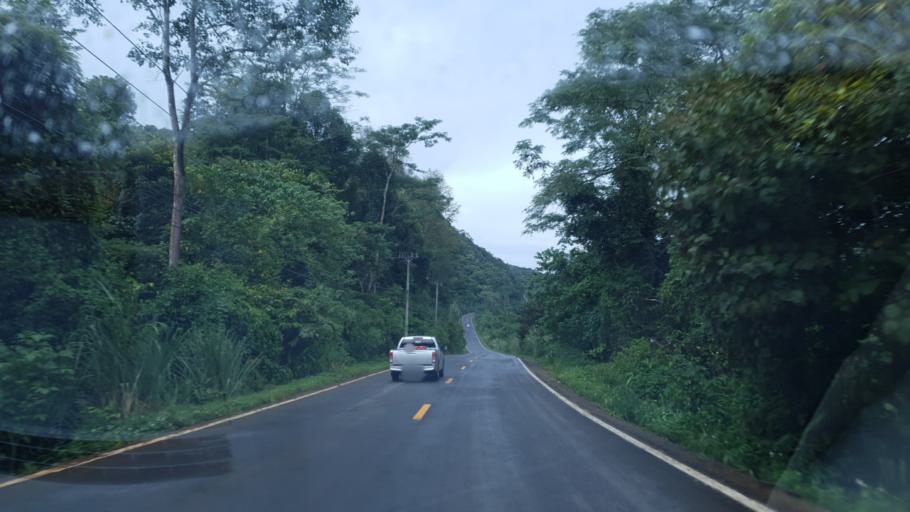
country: TH
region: Mae Hong Son
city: Ban Huai I Huak
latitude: 18.1479
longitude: 98.0989
